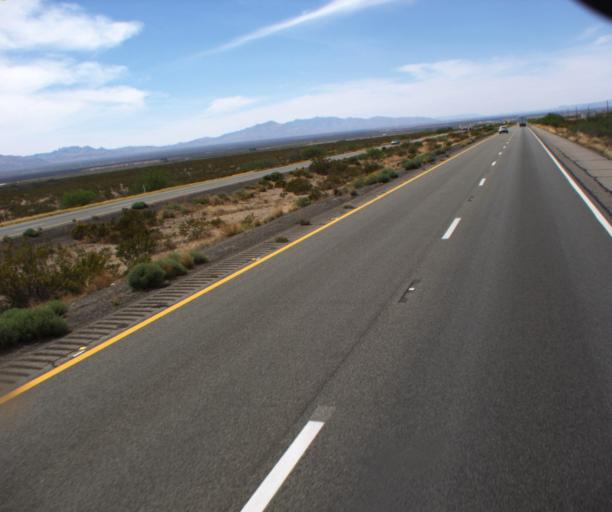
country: US
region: New Mexico
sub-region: Hidalgo County
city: Lordsburg
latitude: 32.2462
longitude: -109.1290
